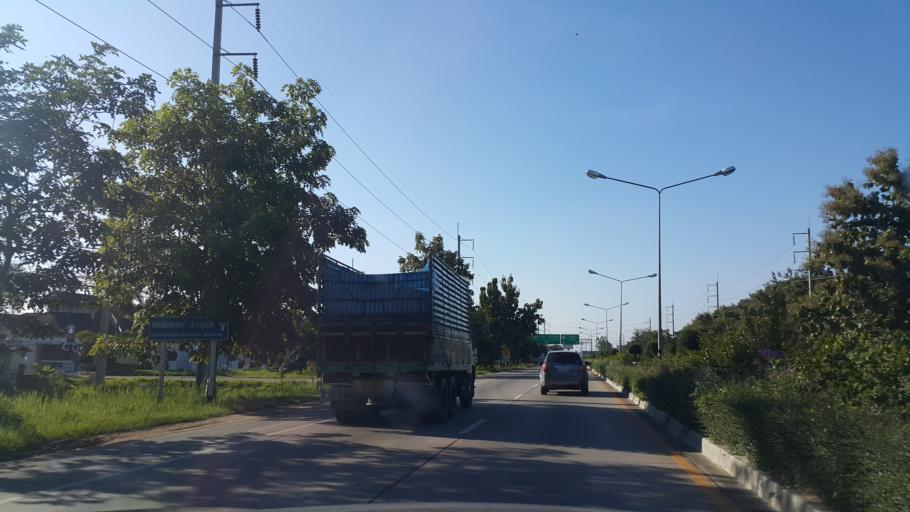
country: TH
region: Lamphun
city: Lamphun
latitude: 18.5544
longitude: 99.0447
